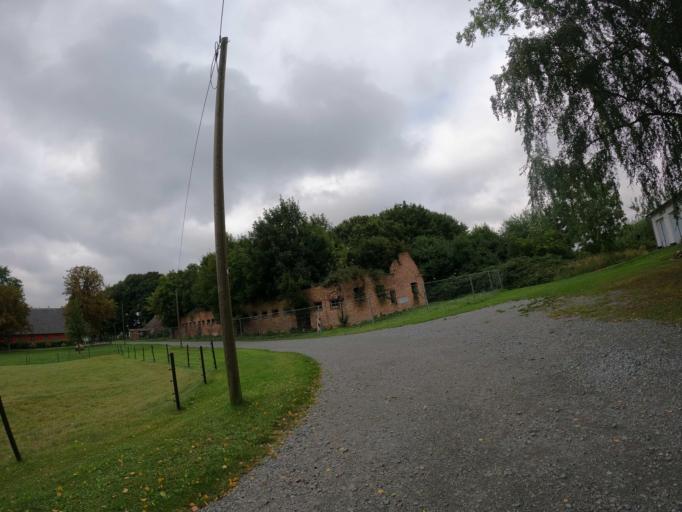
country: DE
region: Mecklenburg-Vorpommern
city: Altefahr
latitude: 54.3215
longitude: 13.1463
